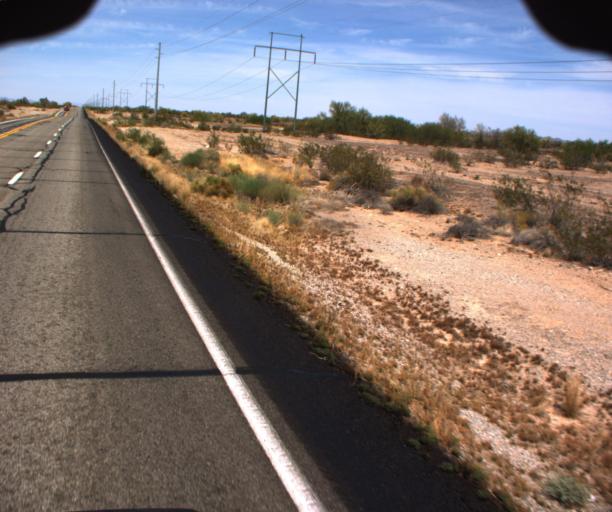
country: US
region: Arizona
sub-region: La Paz County
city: Quartzsite
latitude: 33.7744
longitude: -114.2170
